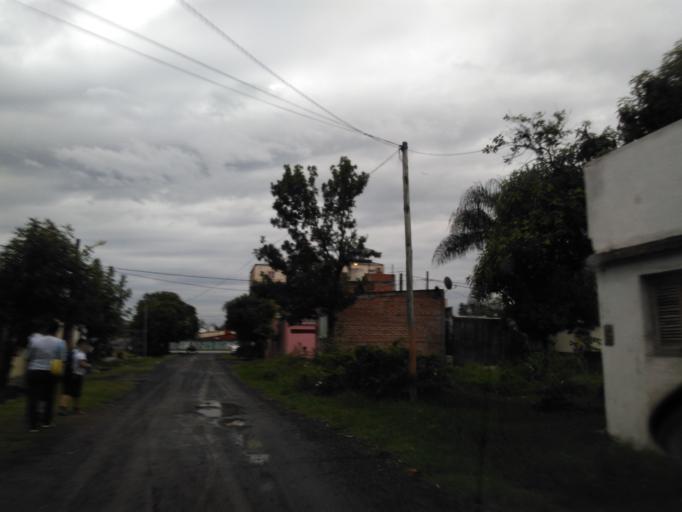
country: AR
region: Chaco
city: Resistencia
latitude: -27.4686
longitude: -58.9797
